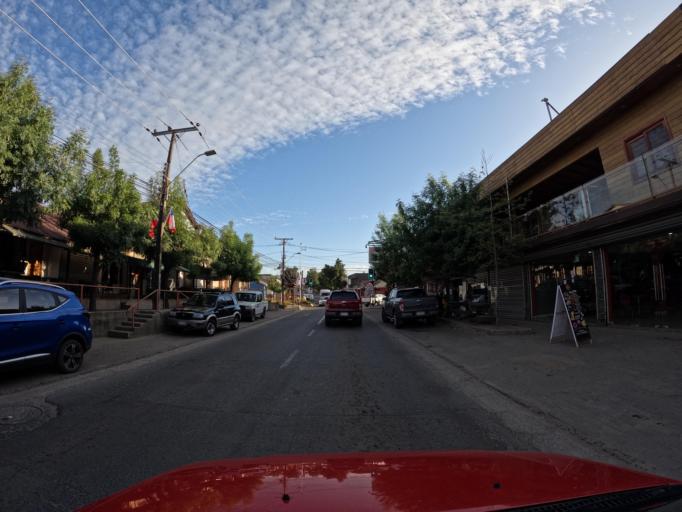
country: CL
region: Valparaiso
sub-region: San Antonio Province
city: San Antonio
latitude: -34.1152
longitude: -71.7264
